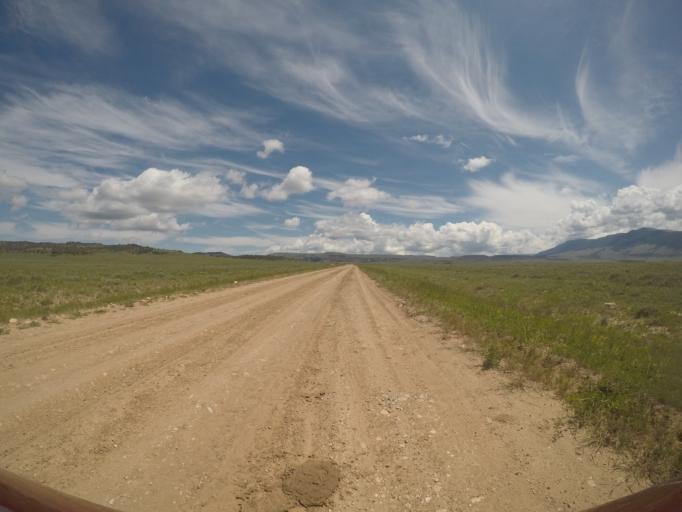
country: US
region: Montana
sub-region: Yellowstone County
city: Laurel
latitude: 45.2330
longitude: -108.6950
